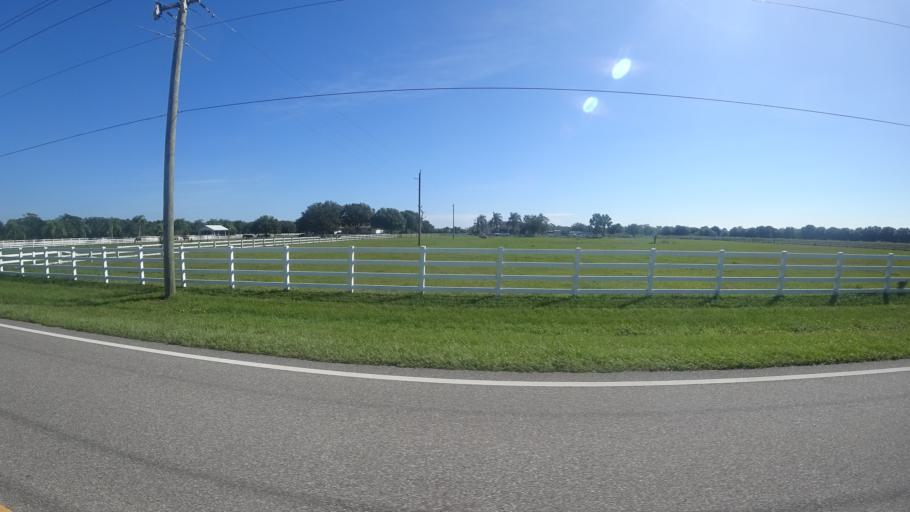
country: US
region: Florida
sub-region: Sarasota County
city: Lake Sarasota
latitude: 27.3636
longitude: -82.2684
